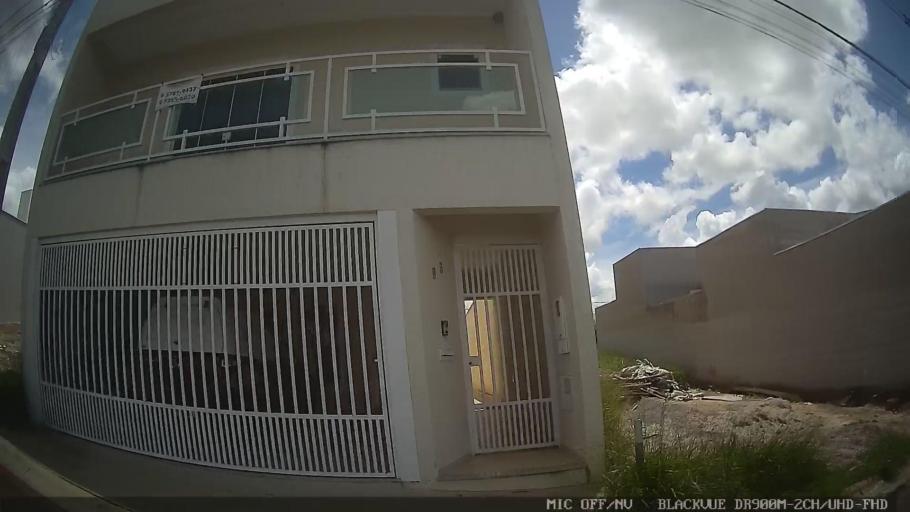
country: BR
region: Sao Paulo
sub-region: Braganca Paulista
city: Braganca Paulista
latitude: -22.9330
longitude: -46.5674
